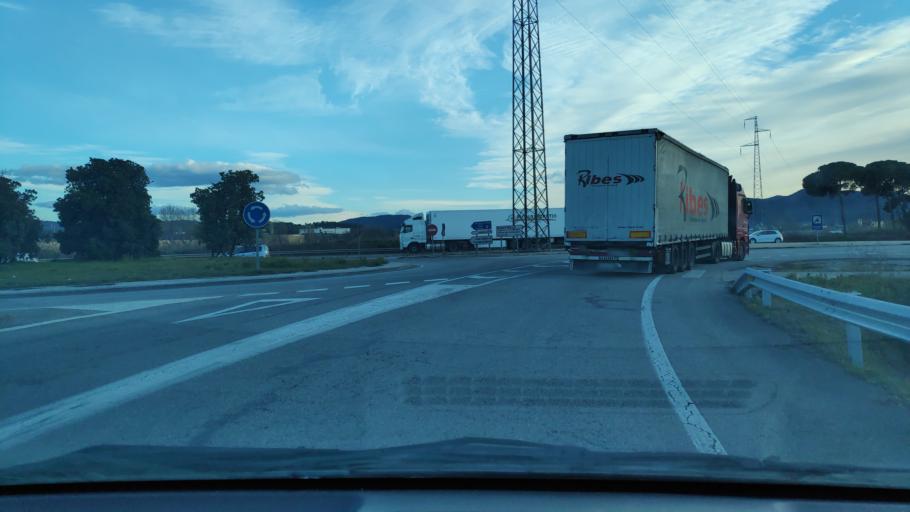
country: ES
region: Catalonia
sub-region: Provincia de Barcelona
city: Llica de Vall
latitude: 41.5752
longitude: 2.2724
